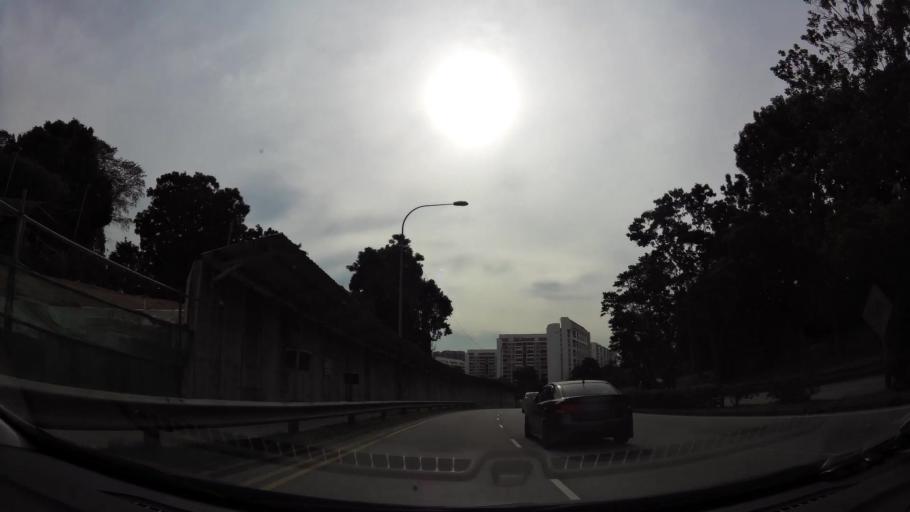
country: SG
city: Singapore
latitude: 1.3251
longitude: 103.7745
